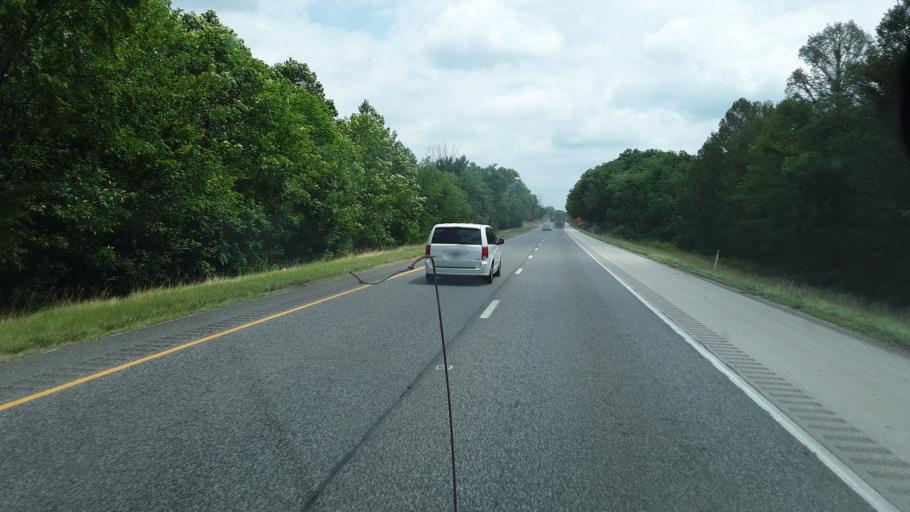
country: US
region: Indiana
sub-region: Clay County
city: Brazil
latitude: 39.4586
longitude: -87.0860
